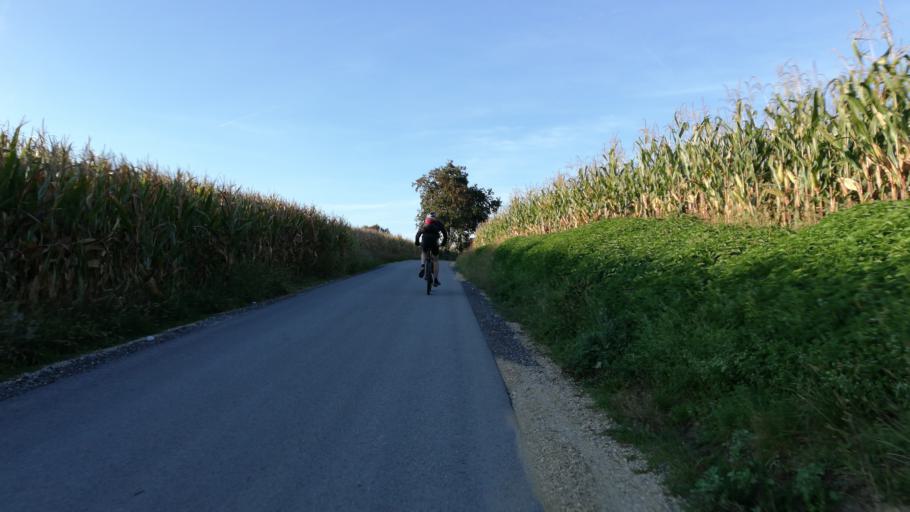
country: AT
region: Upper Austria
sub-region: Wels-Land
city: Edt bei Lambach
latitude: 48.1744
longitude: 13.8934
